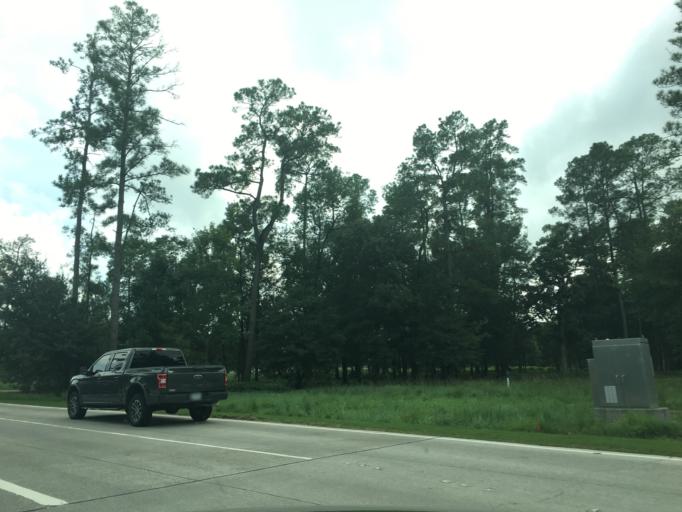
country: US
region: Texas
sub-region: Harris County
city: Spring
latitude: 30.0966
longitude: -95.4517
